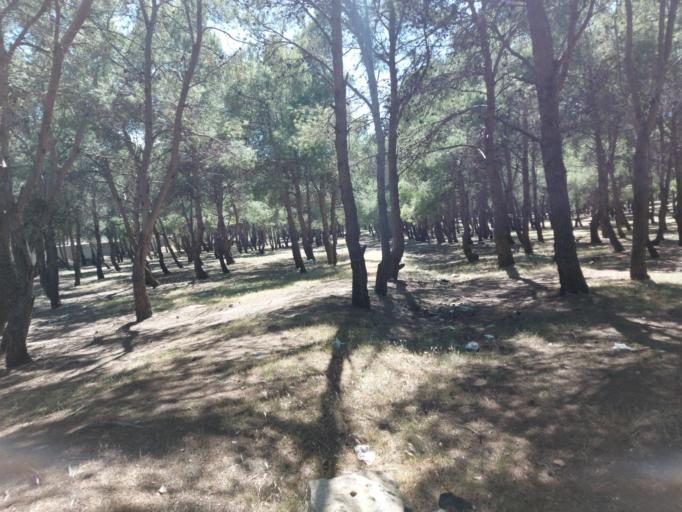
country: TN
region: Kef
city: El Kef
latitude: 36.1850
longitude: 8.7289
